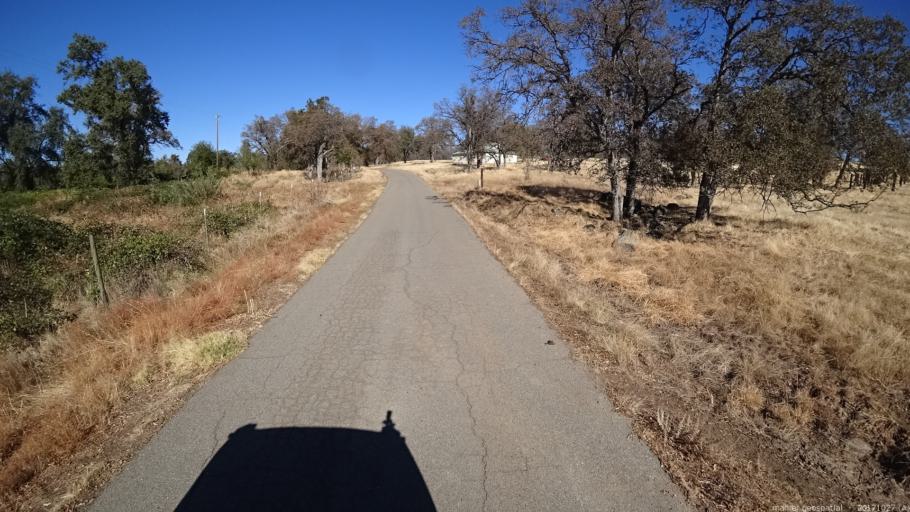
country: US
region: California
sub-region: Shasta County
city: Bella Vista
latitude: 40.6920
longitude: -122.0308
